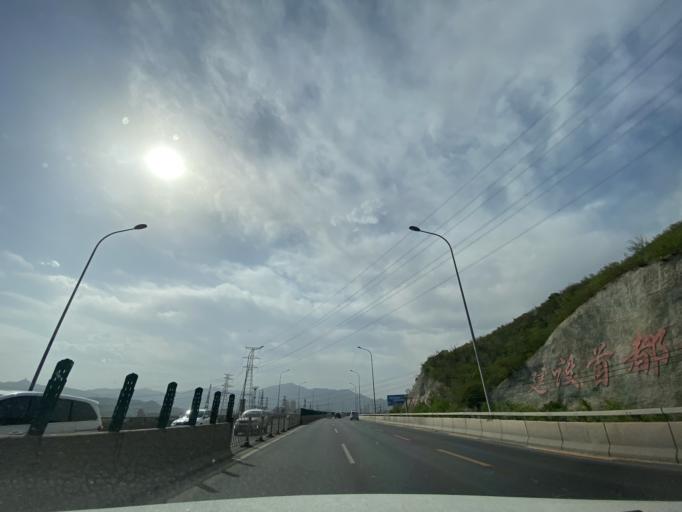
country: CN
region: Beijing
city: Guangning
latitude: 39.9277
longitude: 116.1312
